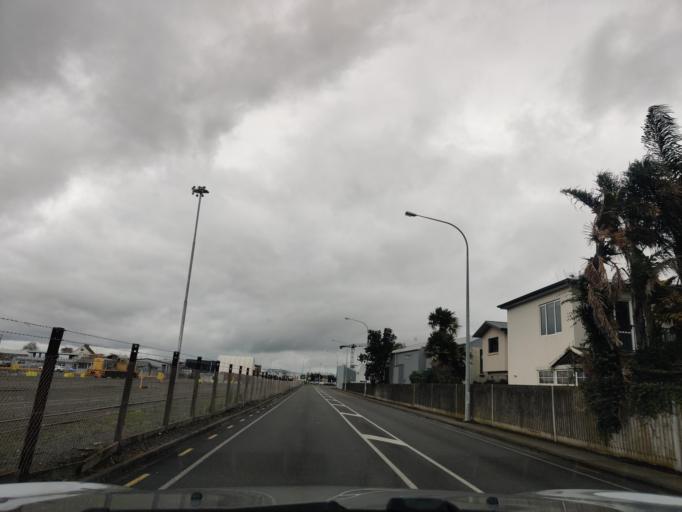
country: NZ
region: Hawke's Bay
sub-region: Napier City
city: Napier
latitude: -39.4807
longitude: 176.9005
